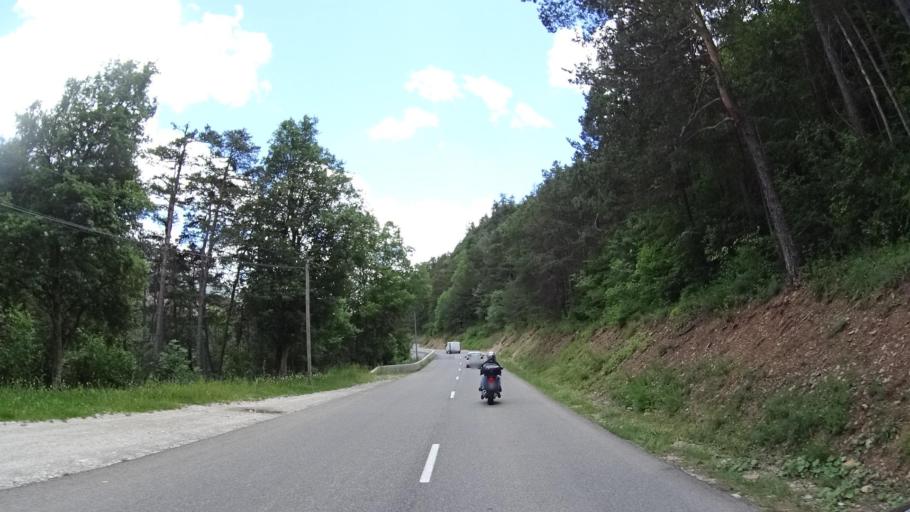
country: FR
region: Provence-Alpes-Cote d'Azur
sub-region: Departement des Alpes-de-Haute-Provence
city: Annot
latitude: 44.0188
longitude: 6.5562
